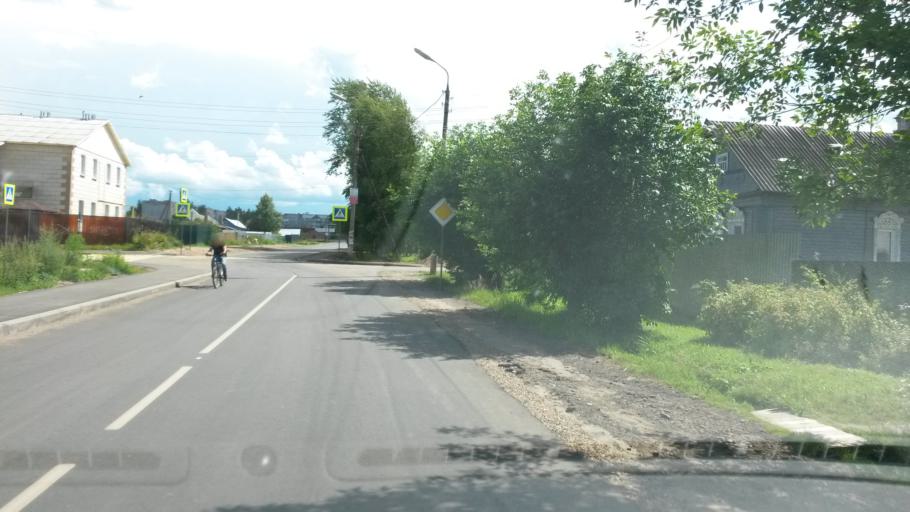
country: RU
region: Jaroslavl
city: Gavrilov-Yam
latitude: 57.3094
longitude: 39.8664
